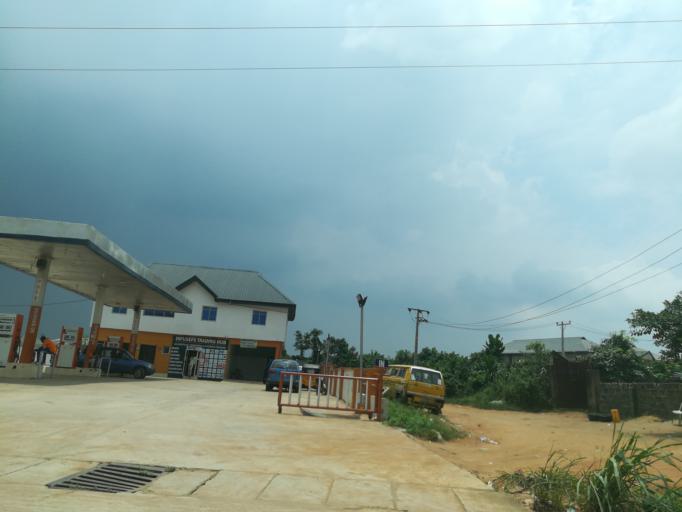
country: NG
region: Lagos
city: Ikorodu
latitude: 6.6122
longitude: 3.5791
